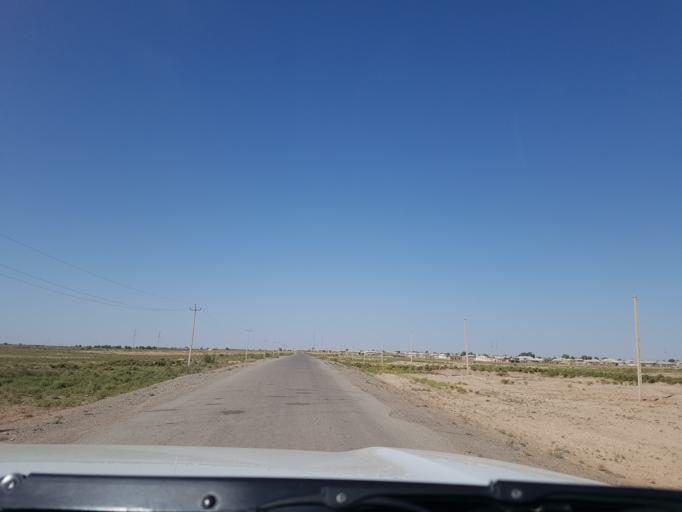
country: IR
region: Razavi Khorasan
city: Sarakhs
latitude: 36.5044
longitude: 61.2534
